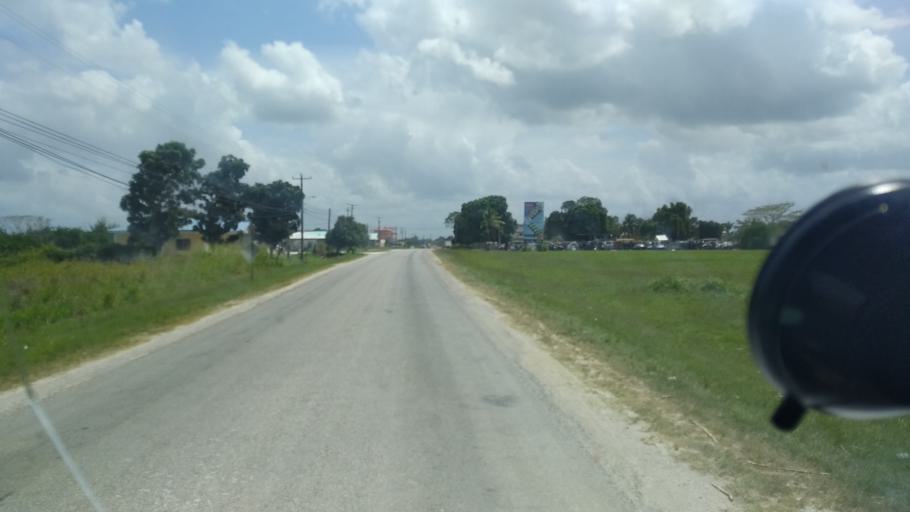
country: BZ
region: Orange Walk
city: Orange Walk
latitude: 18.0603
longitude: -88.5703
